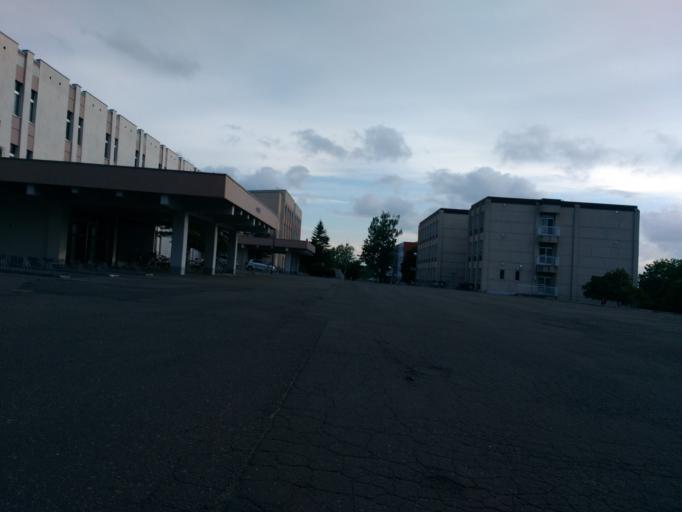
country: JP
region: Hokkaido
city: Ebetsu
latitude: 43.0726
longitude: 141.5090
